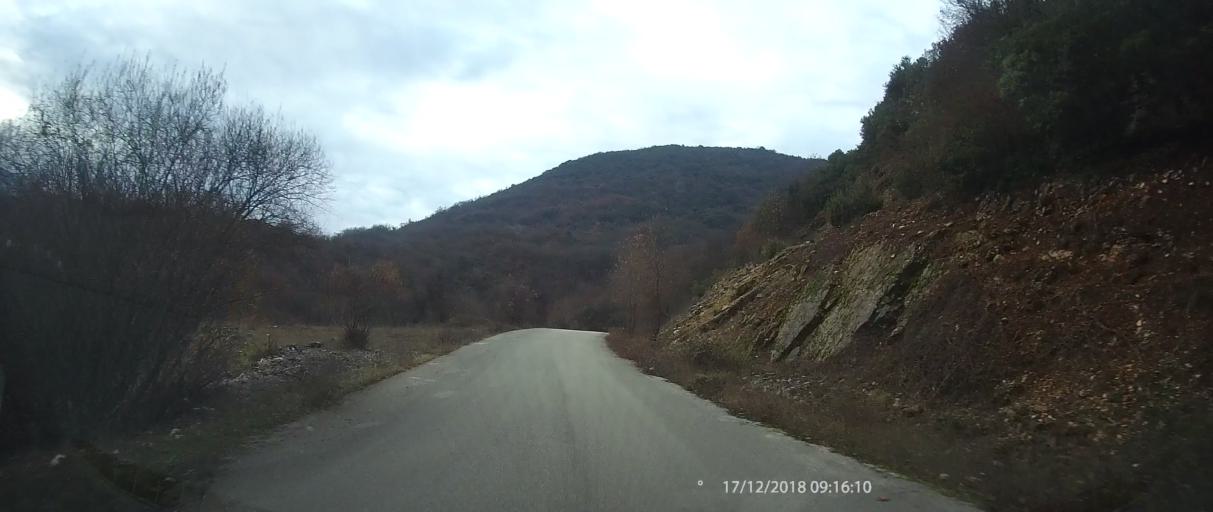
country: GR
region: Epirus
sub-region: Nomos Ioanninon
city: Kalpaki
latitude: 39.9625
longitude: 20.6568
